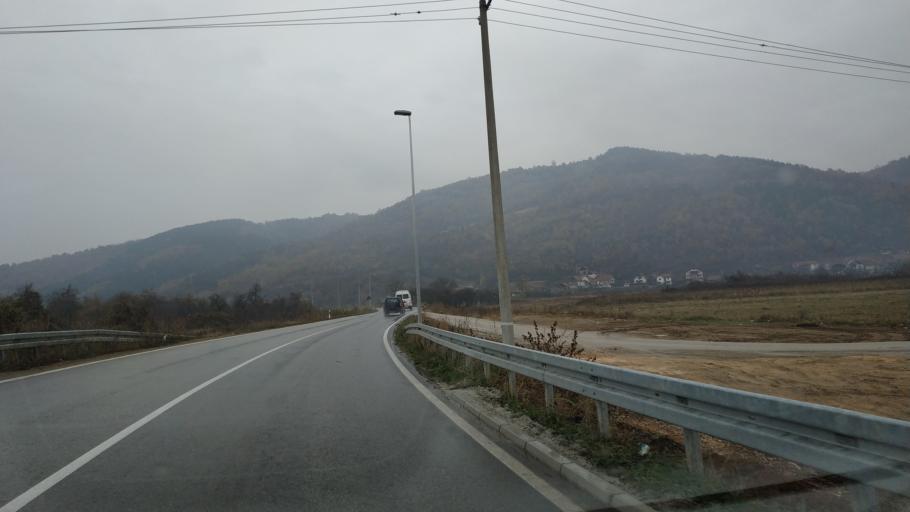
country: RS
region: Central Serbia
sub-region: Pirotski Okrug
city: Pirot
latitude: 43.1831
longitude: 22.5678
